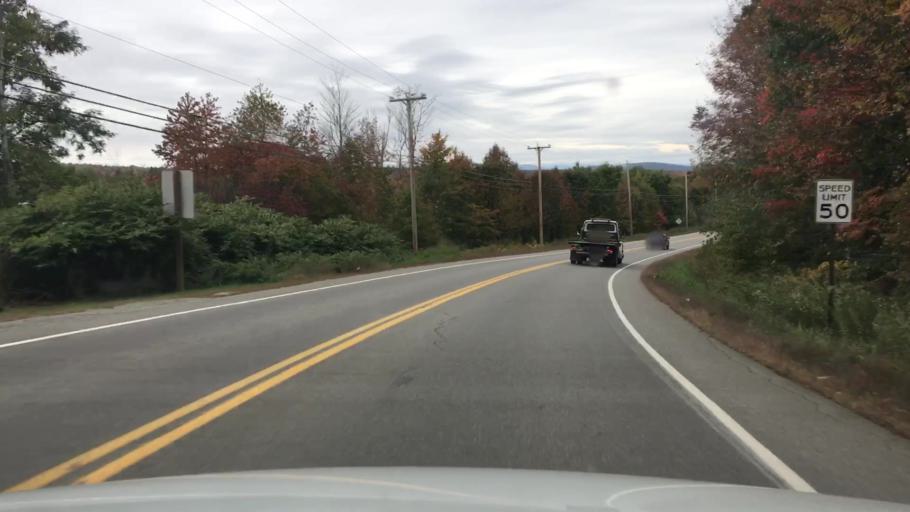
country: US
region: Maine
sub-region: Kennebec County
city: Oakland
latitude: 44.5572
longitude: -69.7424
